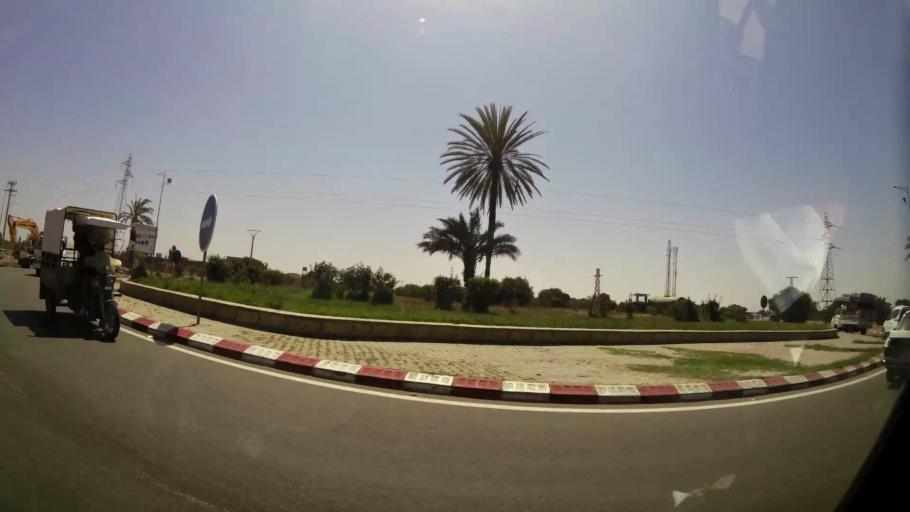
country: MA
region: Souss-Massa-Draa
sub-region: Inezgane-Ait Mellou
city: Inezgane
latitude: 30.3101
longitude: -9.5028
